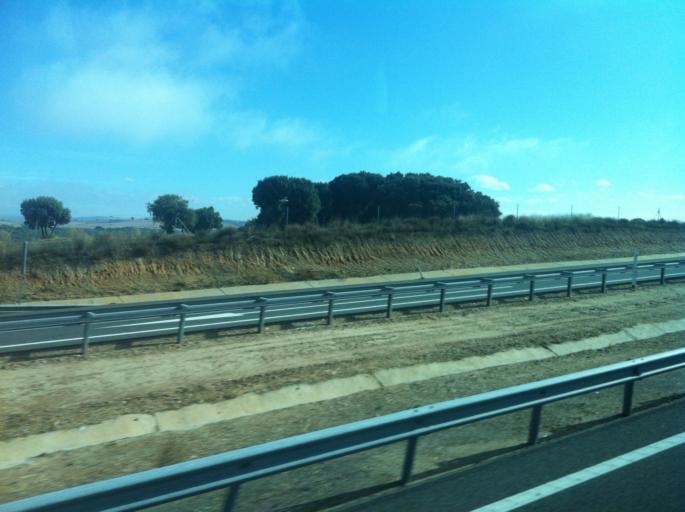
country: ES
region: Castille and Leon
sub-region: Provincia de Burgos
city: Valdorros
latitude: 42.1680
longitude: -3.7027
